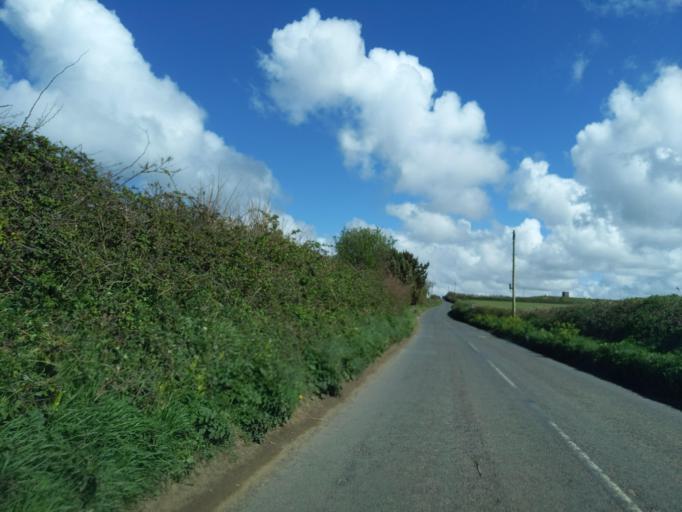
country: GB
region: England
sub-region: Cornwall
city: Wadebridge
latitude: 50.5737
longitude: -4.8387
